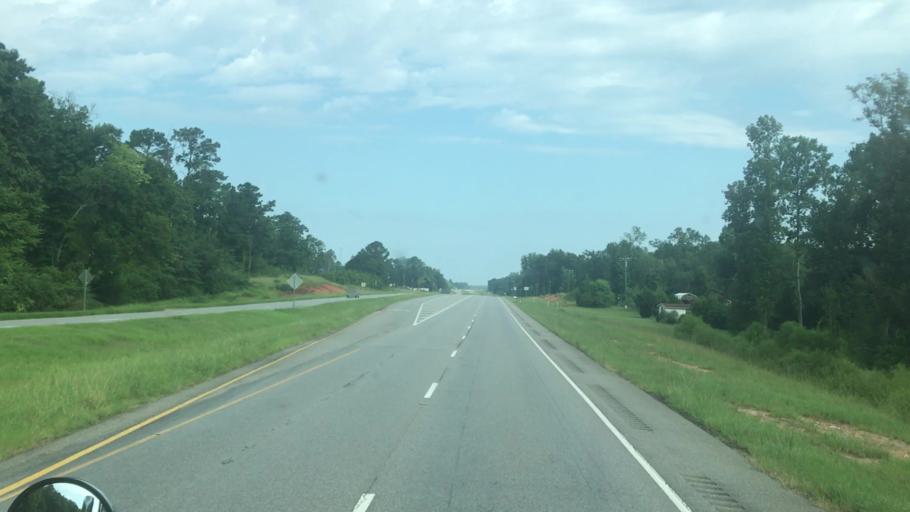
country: US
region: Georgia
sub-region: Early County
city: Blakely
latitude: 31.3339
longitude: -84.8974
